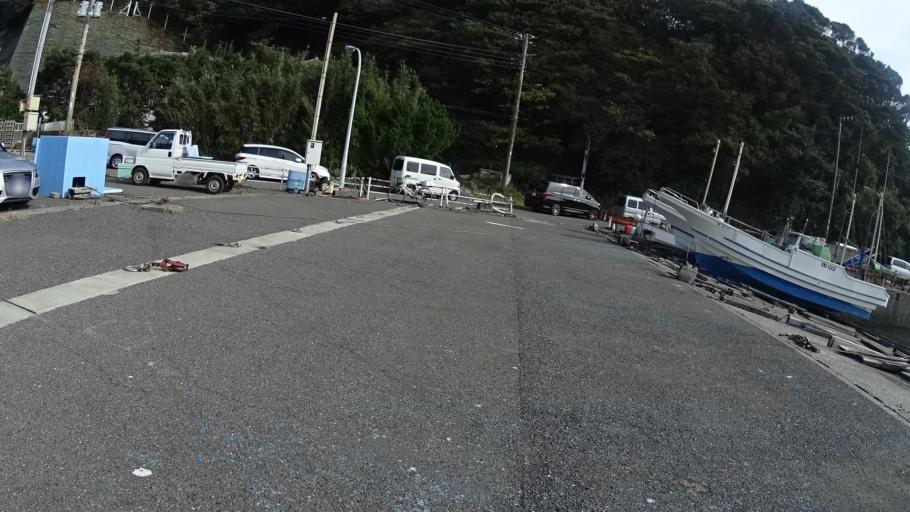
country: JP
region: Kanagawa
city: Miura
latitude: 35.1459
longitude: 139.6774
